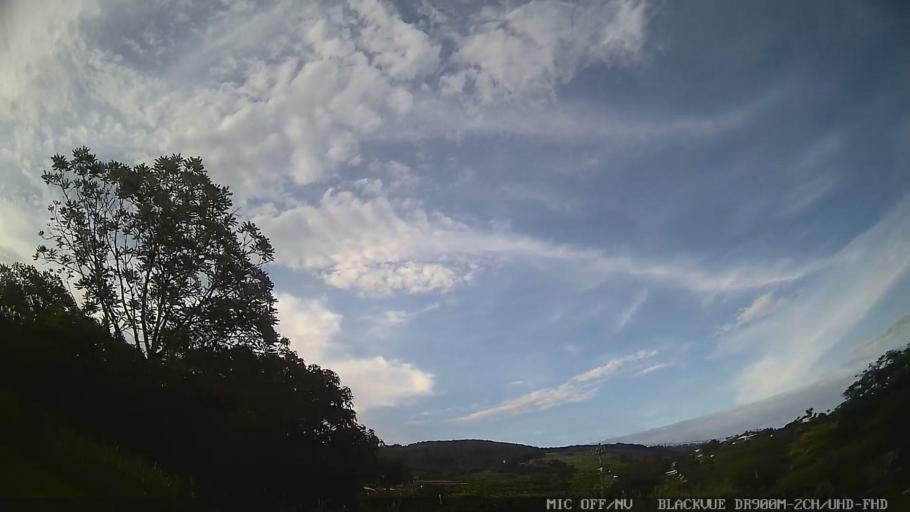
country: BR
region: Sao Paulo
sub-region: Amparo
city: Amparo
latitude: -22.7004
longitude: -46.6965
